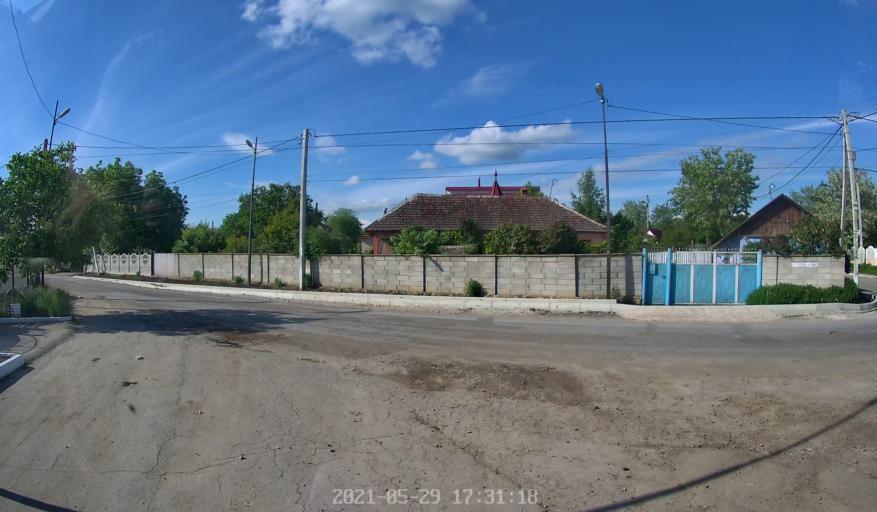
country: MD
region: Laloveni
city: Ialoveni
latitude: 46.8367
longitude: 28.8455
